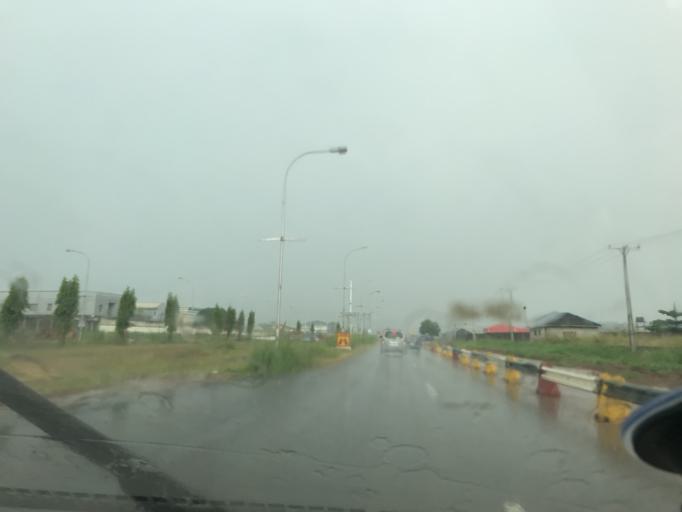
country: NG
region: Lagos
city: Oshodi
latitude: 6.5642
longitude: 3.3215
